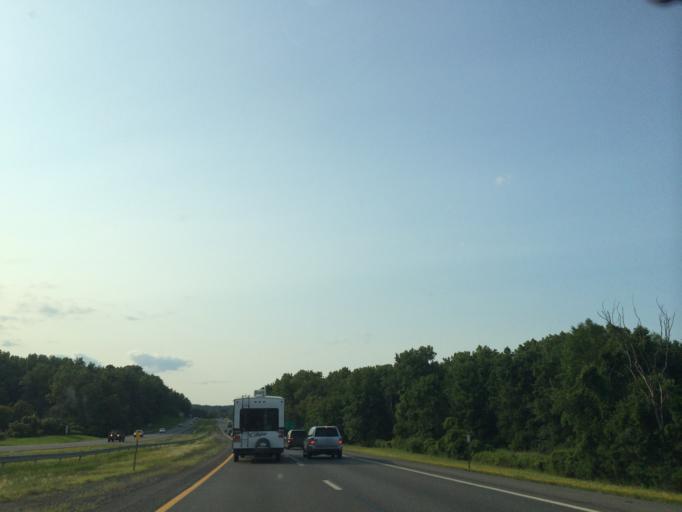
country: US
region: New York
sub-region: Albany County
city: Ravena
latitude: 42.4386
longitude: -73.8046
